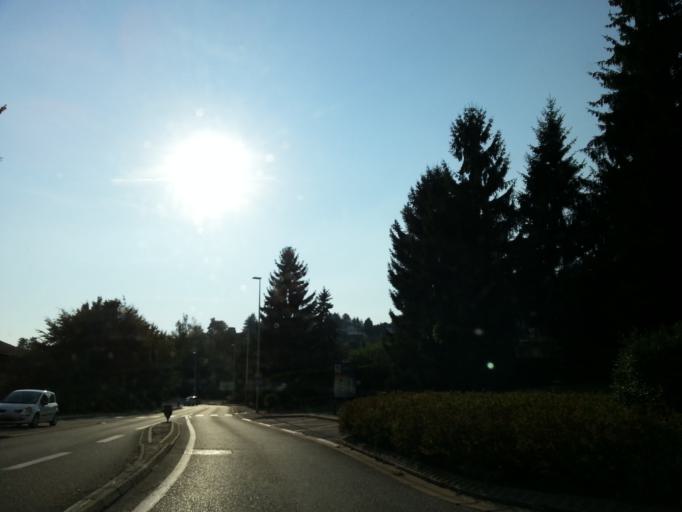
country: FR
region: Rhone-Alpes
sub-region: Departement de la Haute-Savoie
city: Annecy-le-Vieux
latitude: 45.9262
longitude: 6.1516
